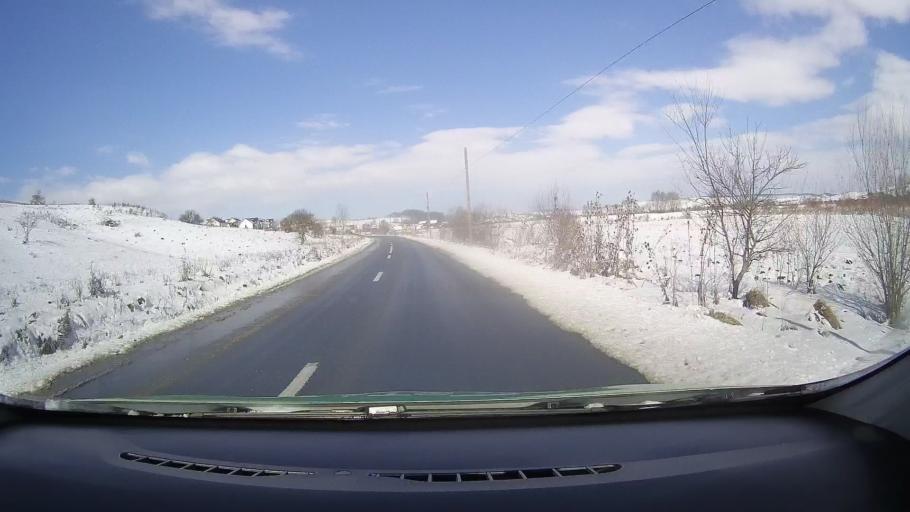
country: RO
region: Sibiu
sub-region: Comuna Nocrich
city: Nocrich
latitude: 45.8815
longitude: 24.4519
